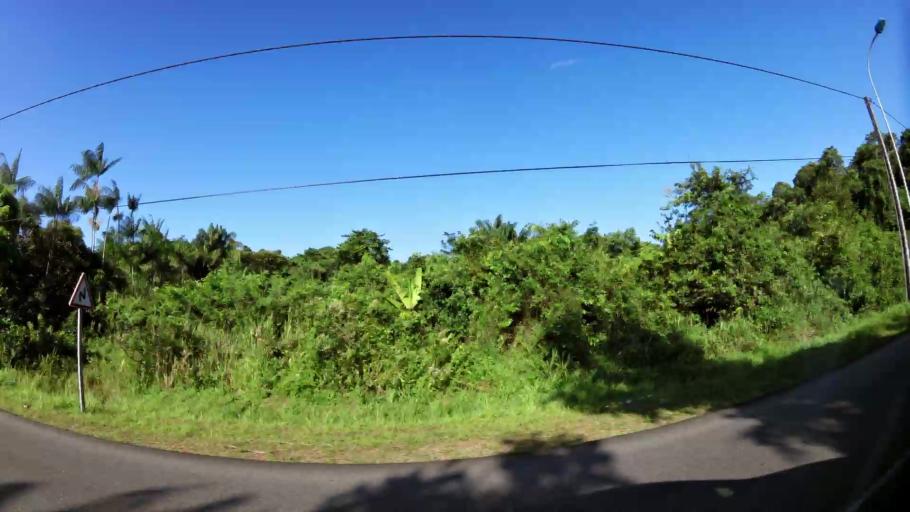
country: GF
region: Guyane
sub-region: Guyane
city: Remire-Montjoly
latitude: 4.9003
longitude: -52.2886
